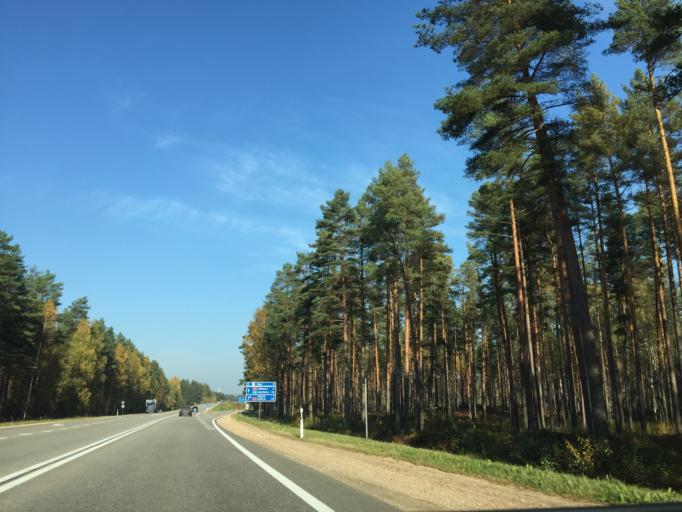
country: LV
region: Babite
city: Pinki
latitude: 56.9163
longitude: 23.9143
